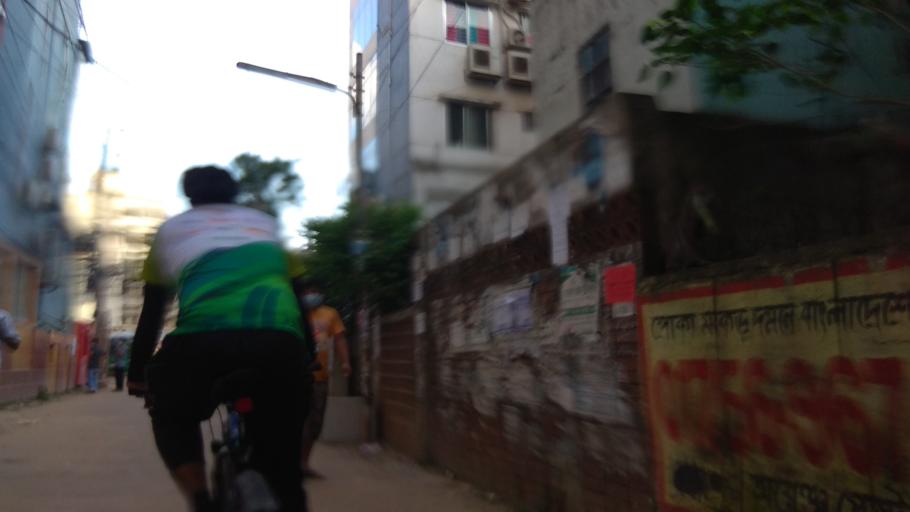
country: BD
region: Dhaka
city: Azimpur
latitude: 23.7749
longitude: 90.3640
